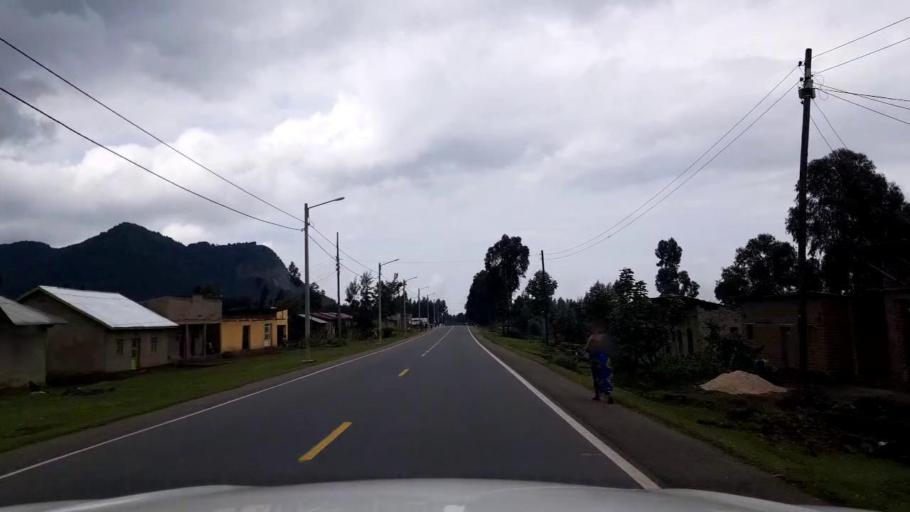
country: RW
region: Western Province
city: Gisenyi
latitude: -1.6356
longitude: 29.4079
